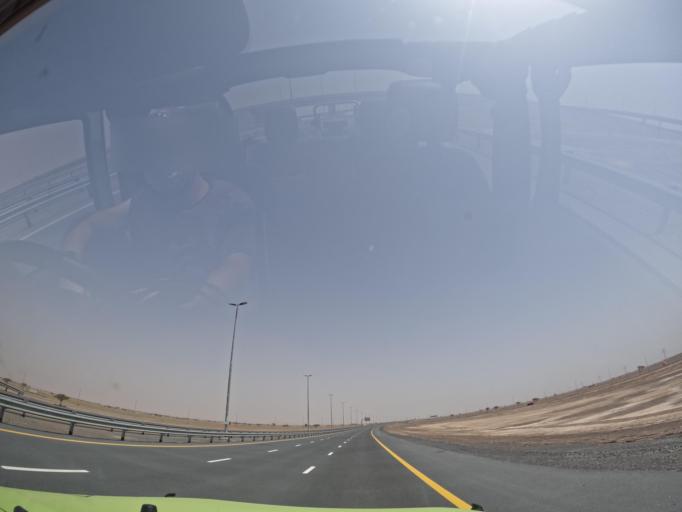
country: AE
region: Ash Shariqah
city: Adh Dhayd
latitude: 24.9114
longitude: 55.8012
